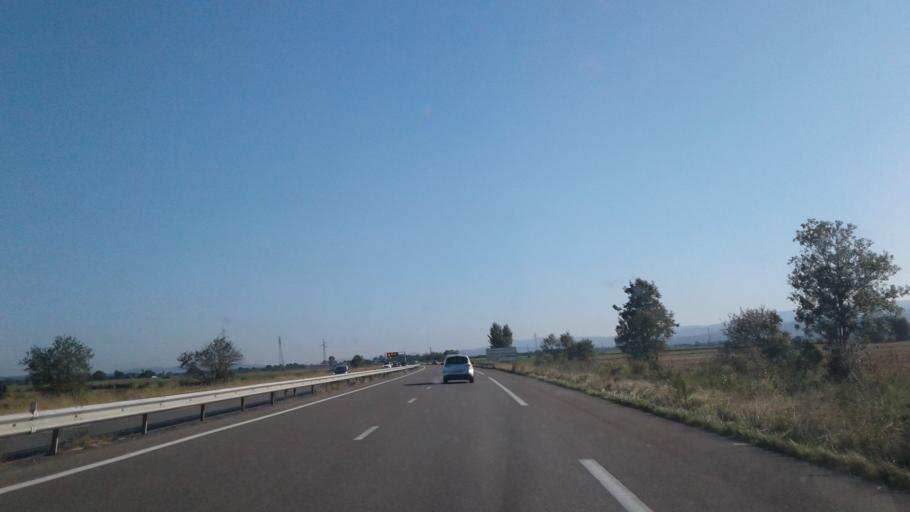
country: FR
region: Rhone-Alpes
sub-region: Departement de l'Ain
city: Chateau-Gaillard
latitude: 45.9484
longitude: 5.3001
